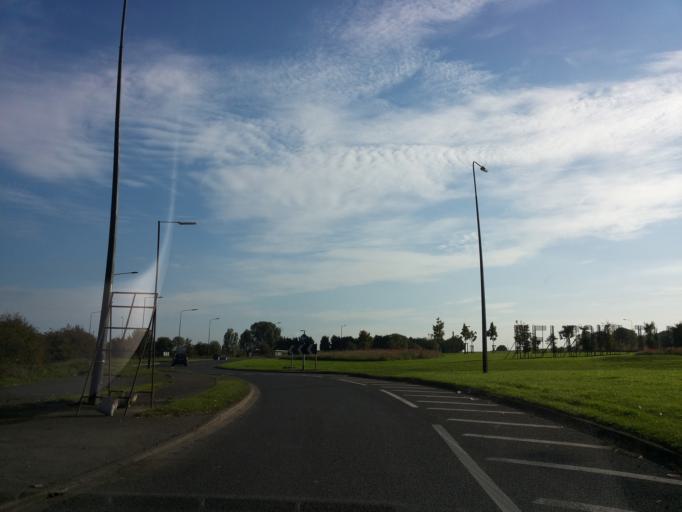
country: GB
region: England
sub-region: Doncaster
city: Hatfield
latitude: 53.5931
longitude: -0.9618
